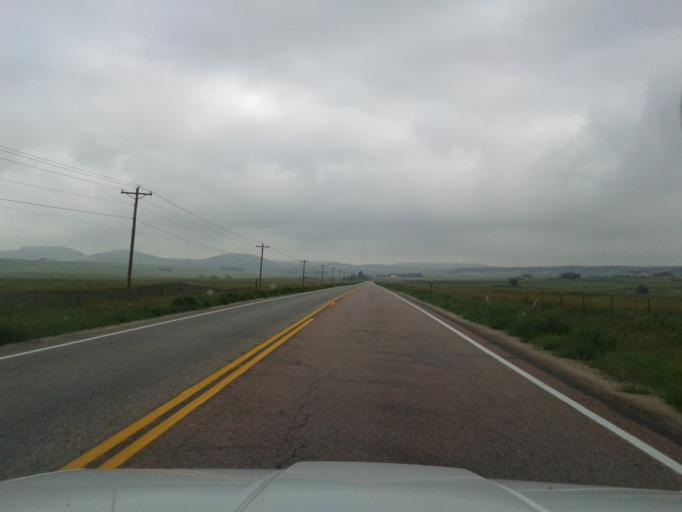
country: US
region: Colorado
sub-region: El Paso County
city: Woodmoor
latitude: 39.1055
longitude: -104.7710
